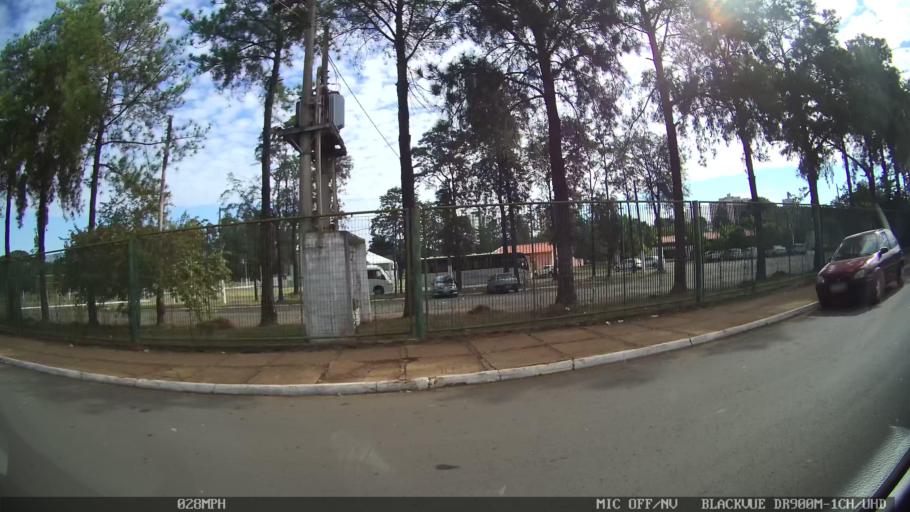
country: BR
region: Sao Paulo
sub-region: Santa Barbara D'Oeste
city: Santa Barbara d'Oeste
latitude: -22.7578
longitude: -47.4072
